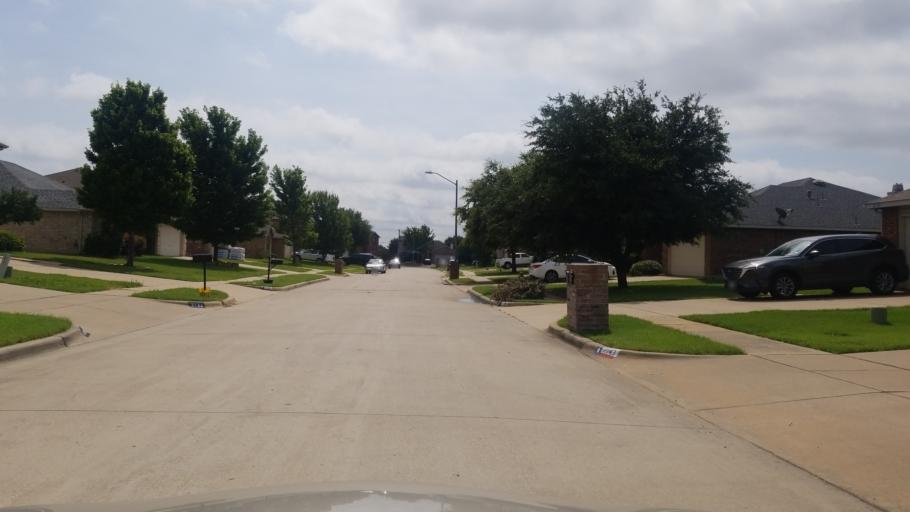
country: US
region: Texas
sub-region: Dallas County
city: Grand Prairie
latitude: 32.6892
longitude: -97.0331
